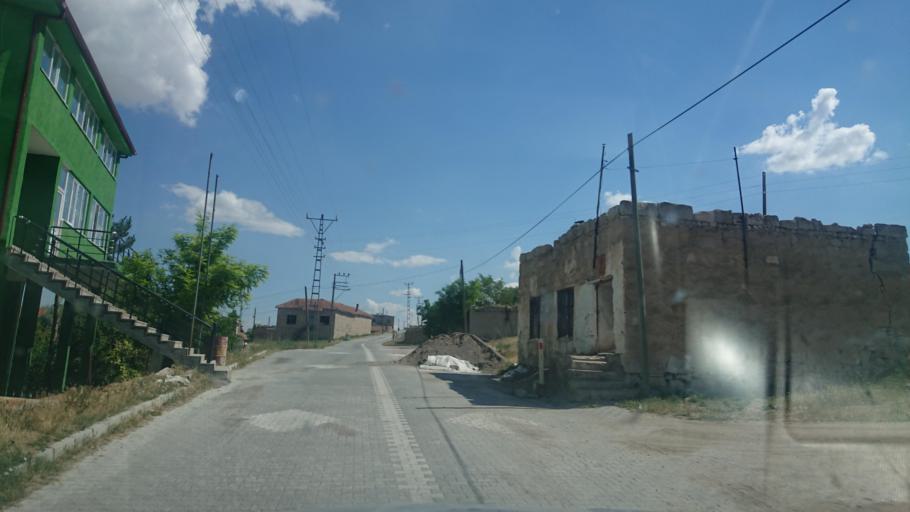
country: TR
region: Aksaray
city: Agacoren
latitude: 38.7713
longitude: 33.7852
